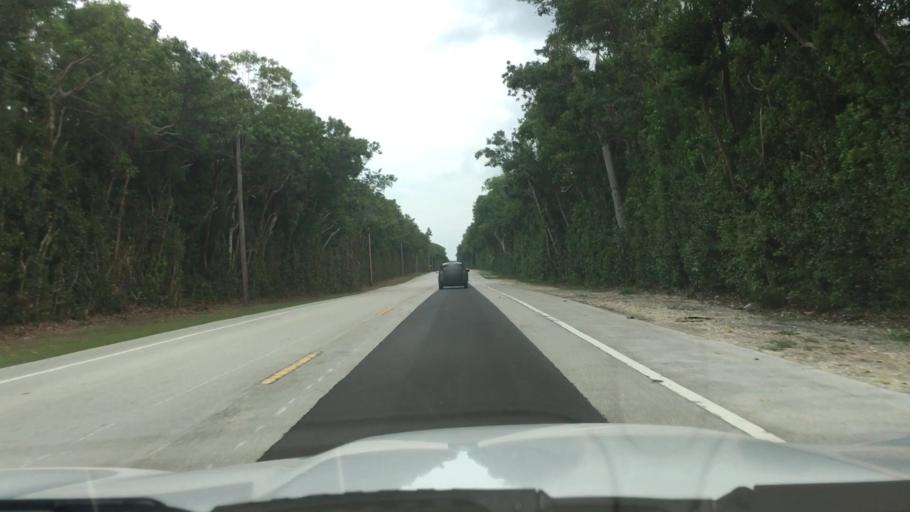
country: US
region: Florida
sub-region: Monroe County
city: North Key Largo
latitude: 25.2433
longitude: -80.3205
